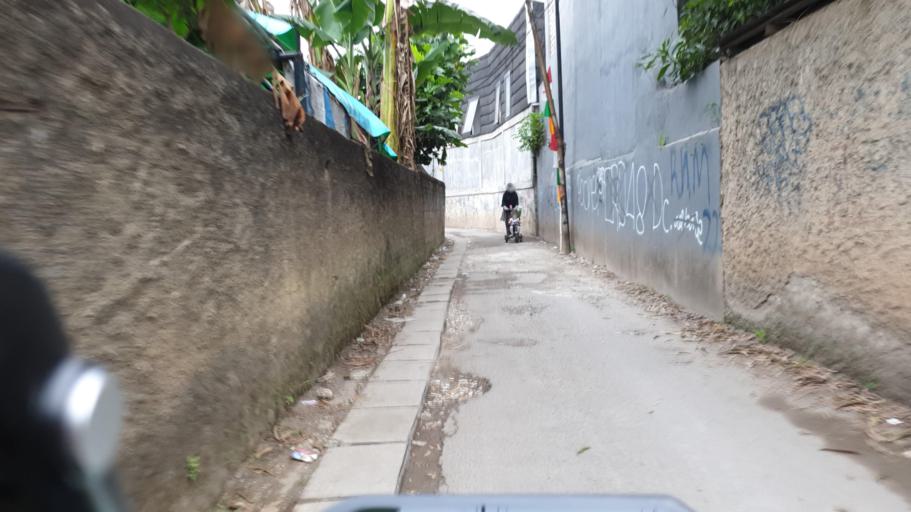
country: ID
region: West Java
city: Pamulang
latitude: -6.3251
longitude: 106.7692
